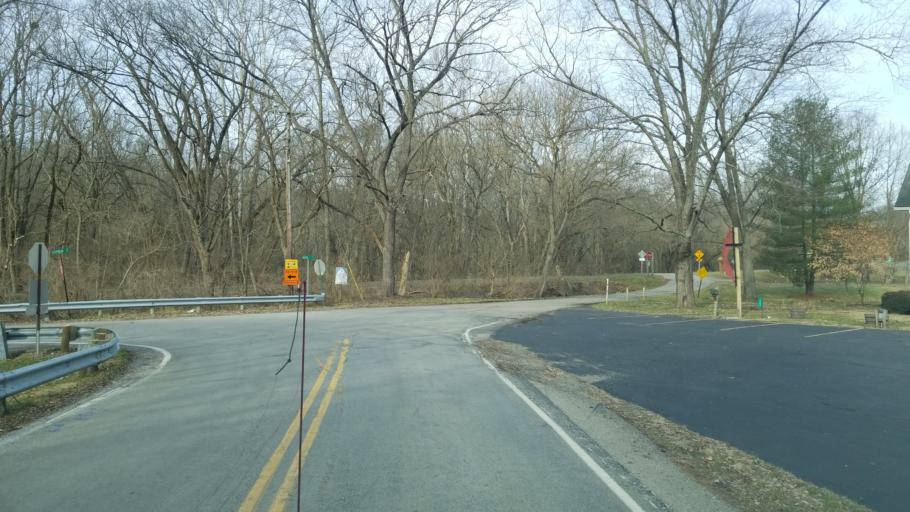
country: US
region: Ohio
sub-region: Warren County
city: Waynesville
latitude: 39.4501
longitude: -84.0966
